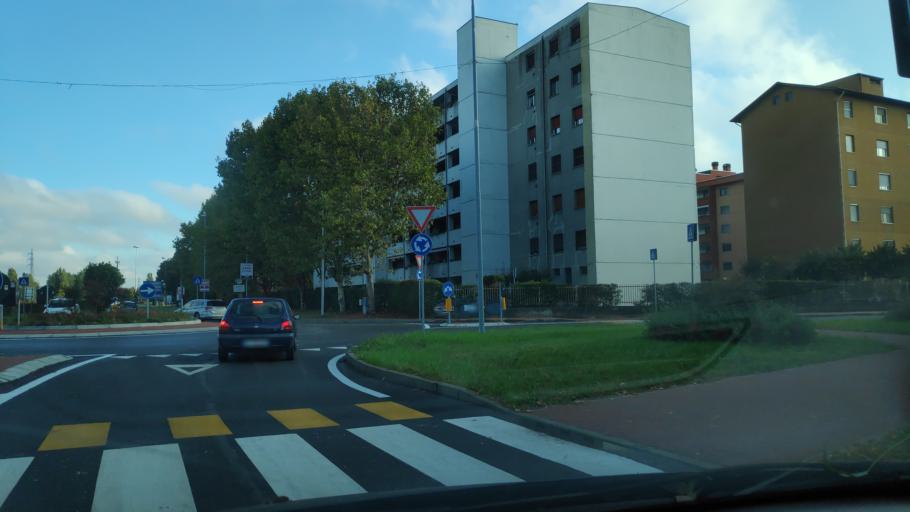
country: IT
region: Lombardy
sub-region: Citta metropolitana di Milano
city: Opera
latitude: 45.3794
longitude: 9.2128
